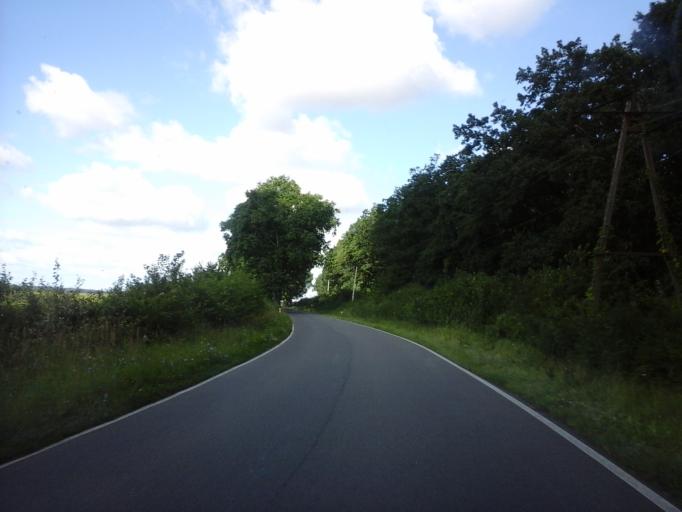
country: PL
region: West Pomeranian Voivodeship
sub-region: Powiat stargardzki
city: Dolice
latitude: 53.1984
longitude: 15.2505
